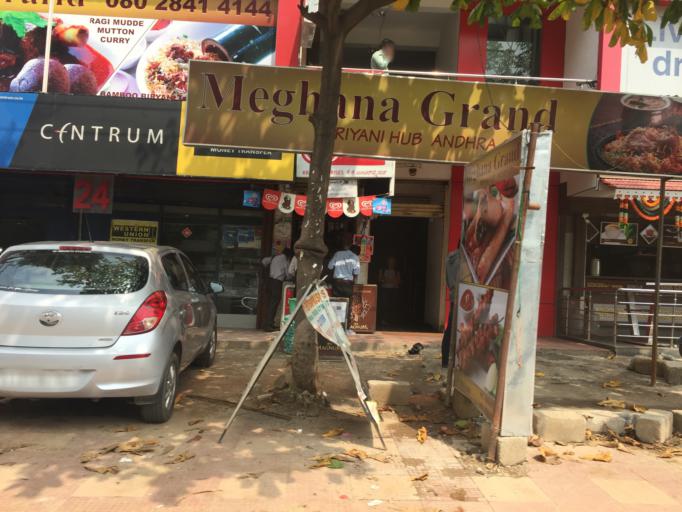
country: IN
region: Karnataka
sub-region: Bangalore Rural
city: Hoskote
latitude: 12.9797
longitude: 77.7272
